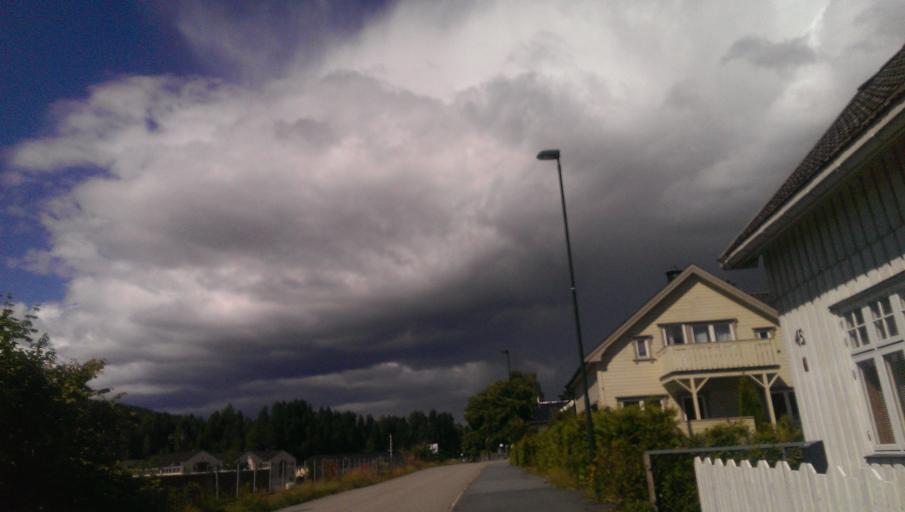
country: NO
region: Buskerud
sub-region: Kongsberg
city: Kongsberg
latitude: 59.6566
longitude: 9.6532
